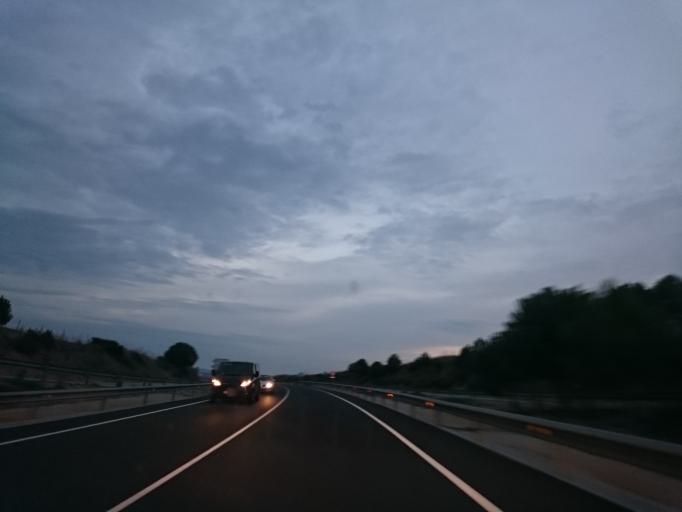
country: ES
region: Catalonia
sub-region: Provincia de Barcelona
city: Sant Pere de Riudebitlles
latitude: 41.4298
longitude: 1.6800
